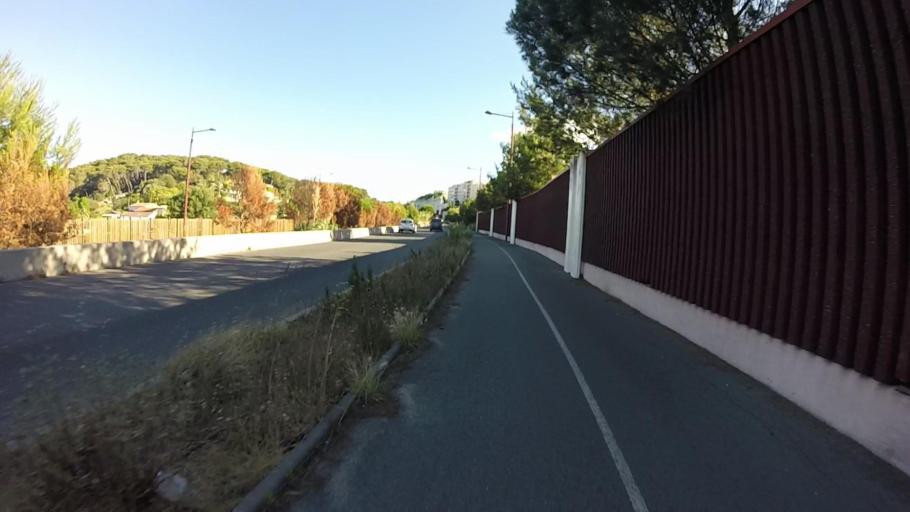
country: FR
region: Provence-Alpes-Cote d'Azur
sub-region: Departement des Alpes-Maritimes
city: Biot
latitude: 43.5899
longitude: 7.0924
